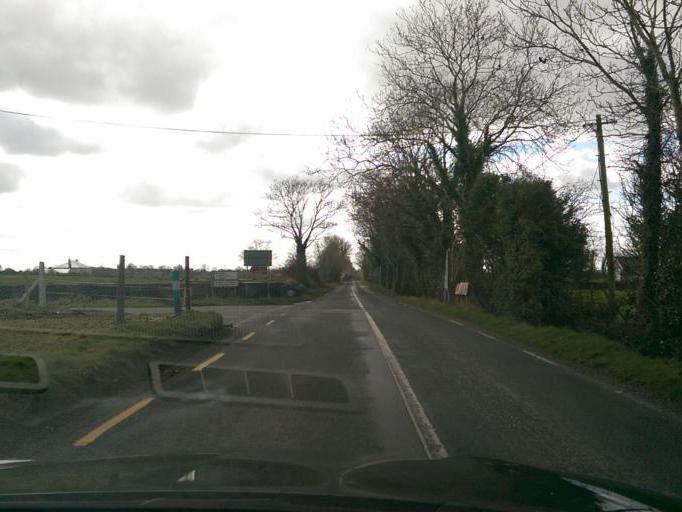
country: IE
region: Connaught
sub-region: County Galway
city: Athenry
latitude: 53.4068
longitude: -8.6363
